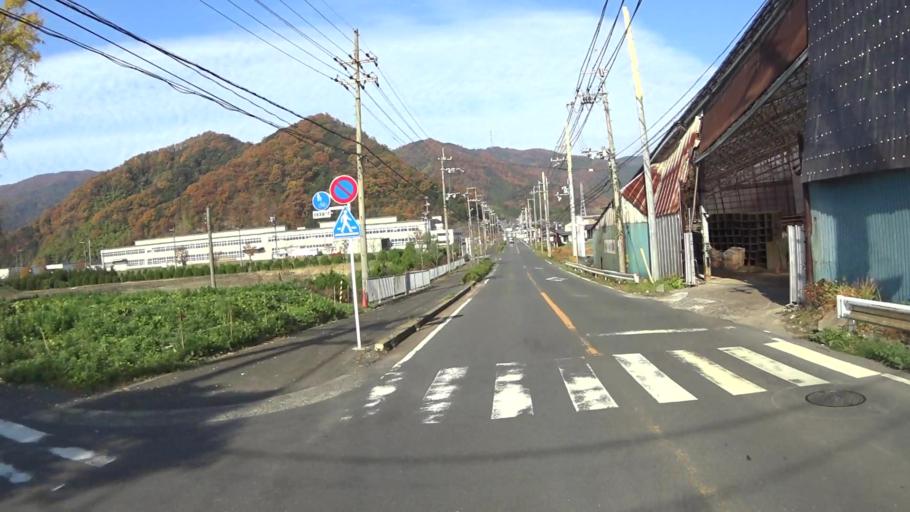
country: JP
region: Kyoto
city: Maizuru
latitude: 35.5131
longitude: 135.4016
